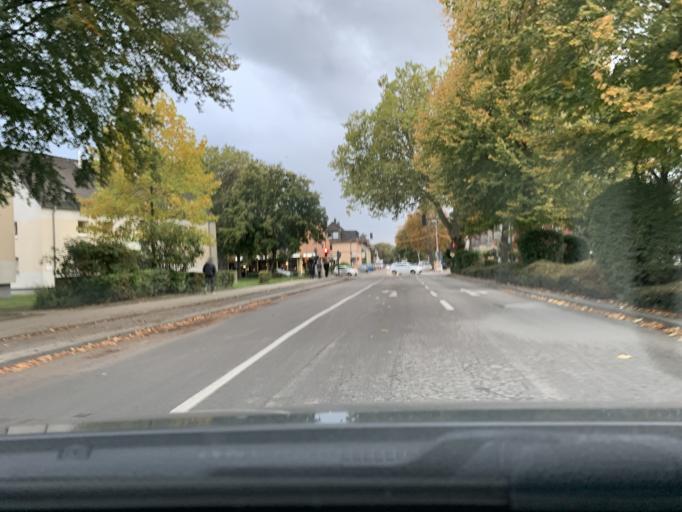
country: DE
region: North Rhine-Westphalia
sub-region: Regierungsbezirk Dusseldorf
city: Oberhausen
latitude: 51.4726
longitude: 6.9243
